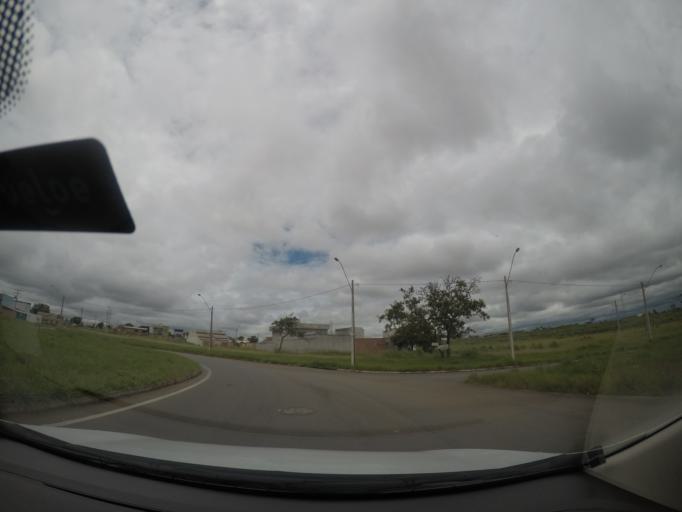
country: BR
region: Goias
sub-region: Goiania
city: Goiania
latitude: -16.7480
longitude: -49.3379
